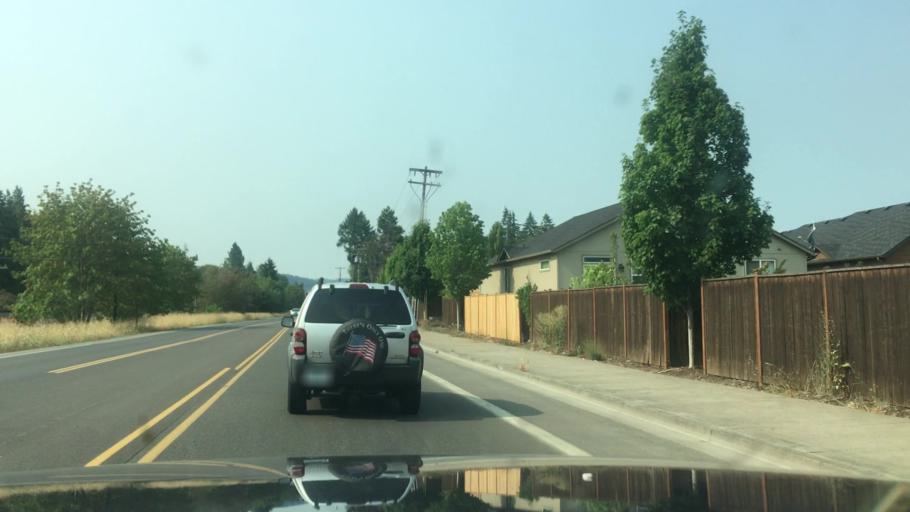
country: US
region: Oregon
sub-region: Lane County
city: Cottage Grove
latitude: 43.7875
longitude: -123.0662
